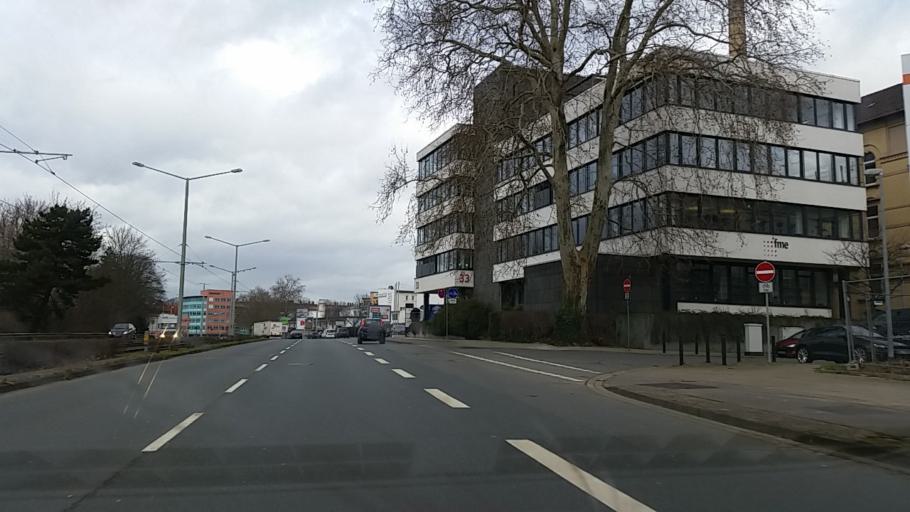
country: DE
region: Lower Saxony
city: Braunschweig
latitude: 52.2483
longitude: 10.5296
